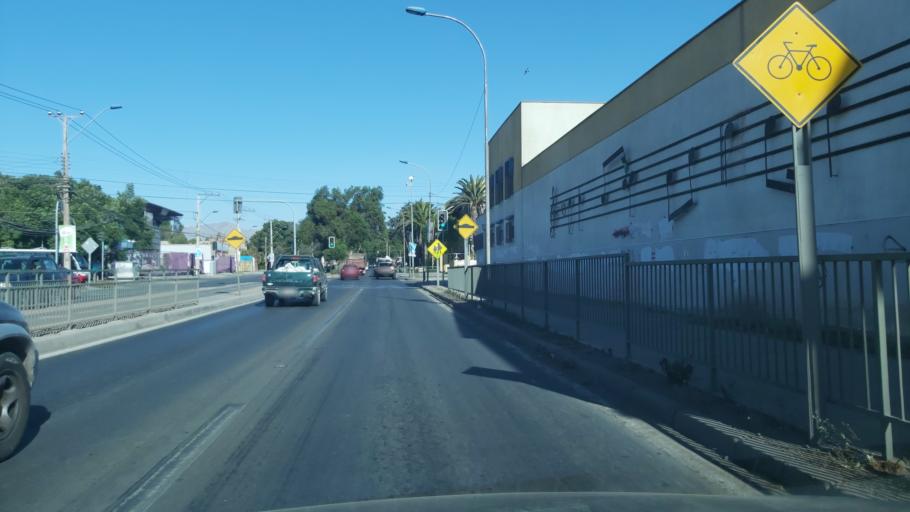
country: CL
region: Atacama
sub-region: Provincia de Copiapo
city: Copiapo
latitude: -27.3737
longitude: -70.3283
